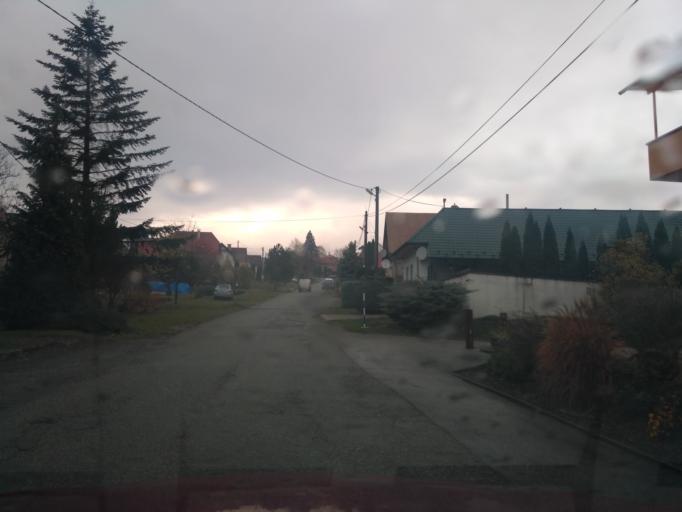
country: SK
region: Kosicky
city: Moldava nad Bodvou
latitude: 48.6755
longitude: 21.1136
